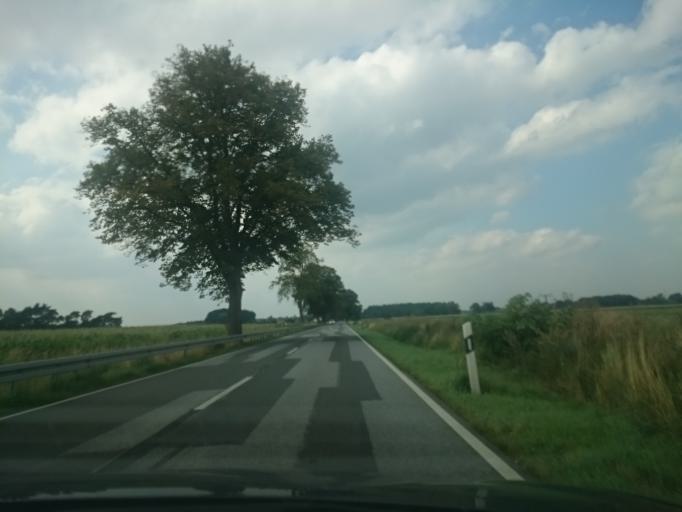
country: DE
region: Mecklenburg-Vorpommern
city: Ferdinandshof
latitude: 53.6972
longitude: 13.8707
